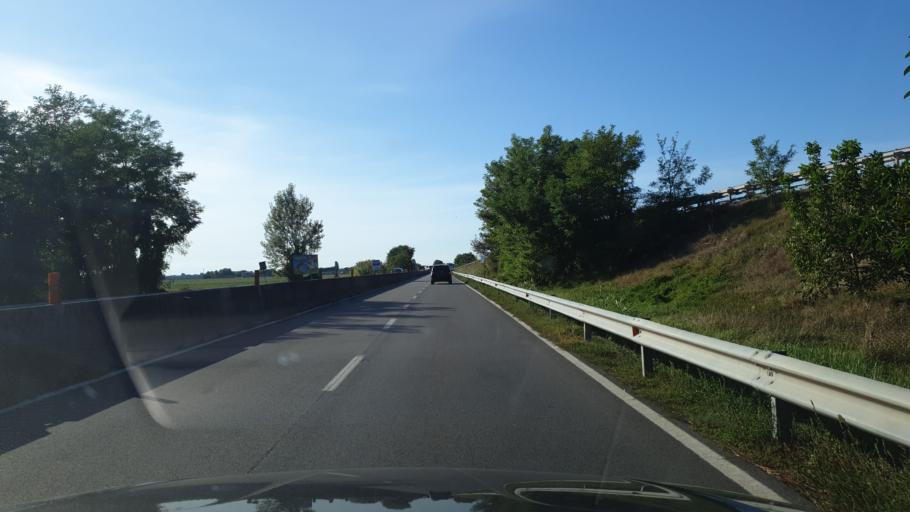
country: IT
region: Emilia-Romagna
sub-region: Provincia di Ravenna
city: Classe
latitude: 44.3723
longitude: 12.2364
